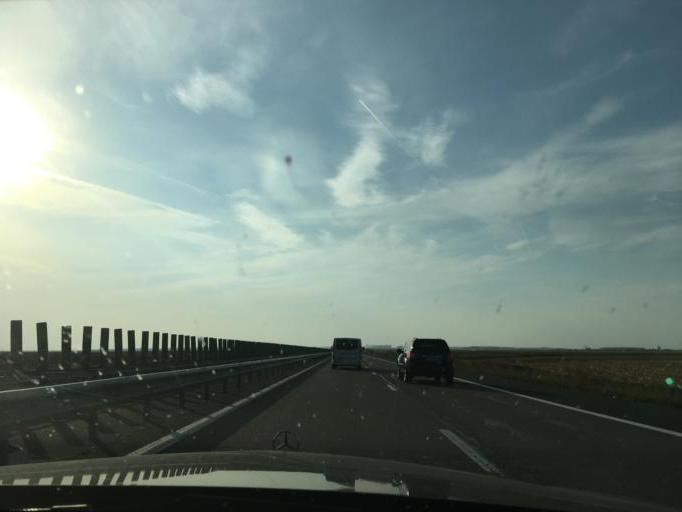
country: RO
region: Calarasi
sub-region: Comuna Dor Marunt
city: Dor Marunt
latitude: 44.4259
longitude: 26.9319
